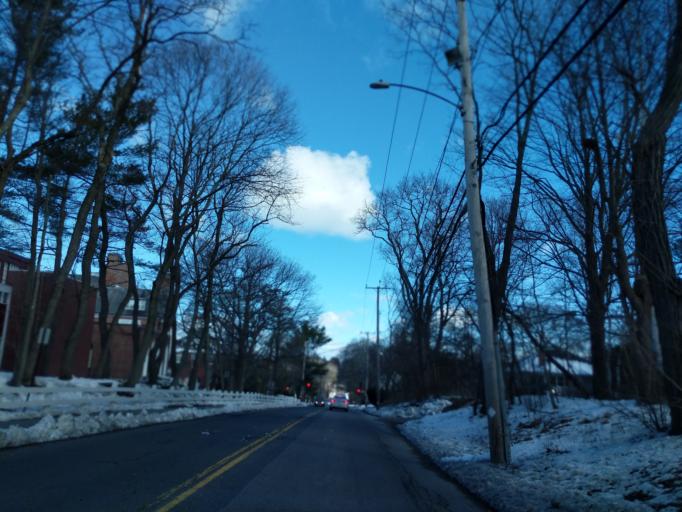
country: US
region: Massachusetts
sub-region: Norfolk County
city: Milton
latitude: 42.2555
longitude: -71.0688
